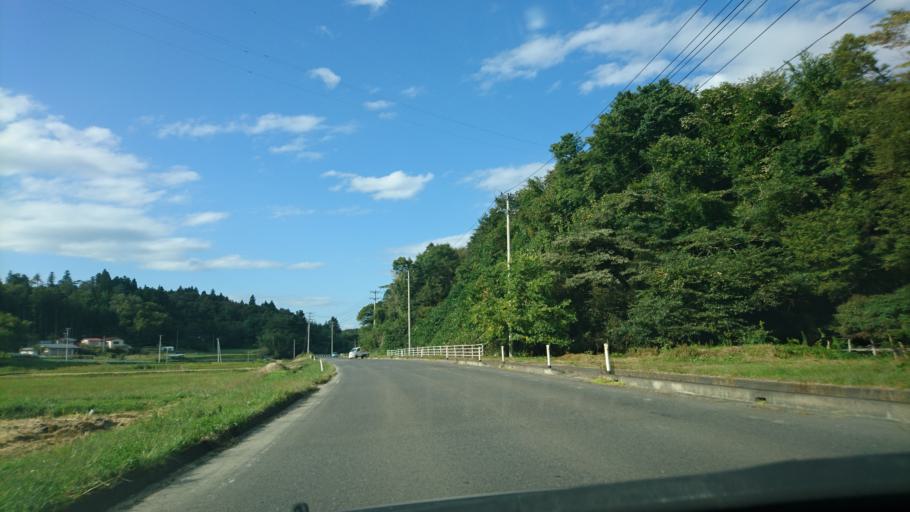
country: JP
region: Iwate
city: Ichinoseki
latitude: 38.8877
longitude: 141.3324
